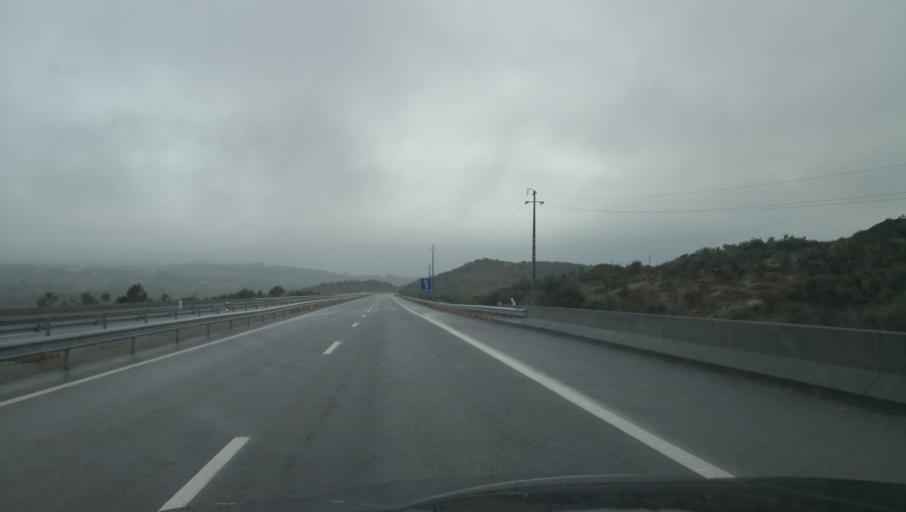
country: PT
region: Vila Real
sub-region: Vila Real
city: Vila Real
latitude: 41.3811
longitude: -7.6660
